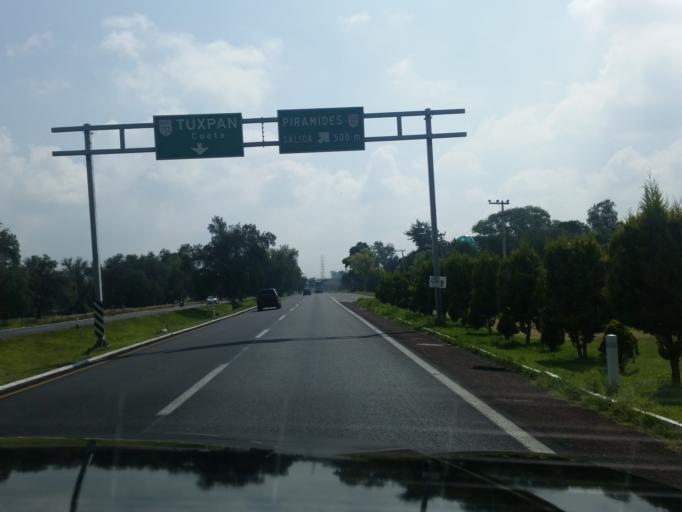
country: MX
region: Morelos
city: Xometla
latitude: 19.6510
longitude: -98.8847
